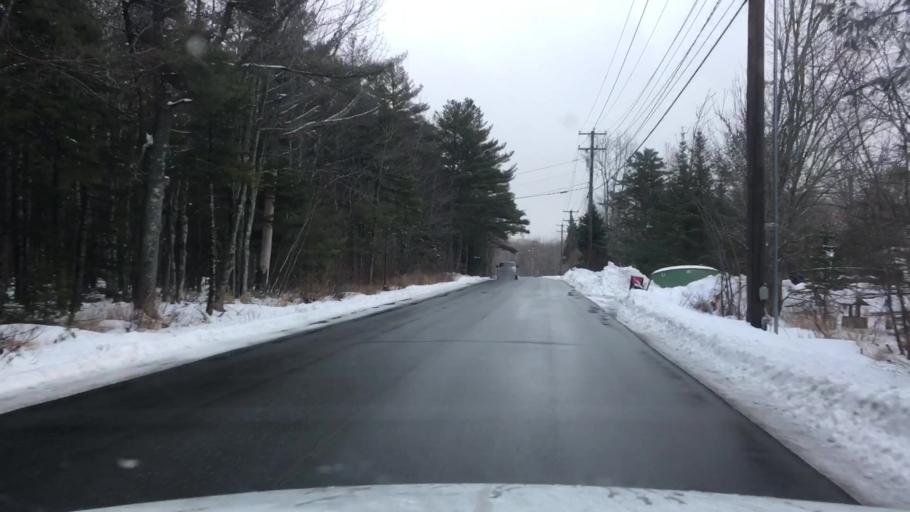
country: US
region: Maine
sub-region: Hancock County
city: Trenton
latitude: 44.4097
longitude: -68.3311
